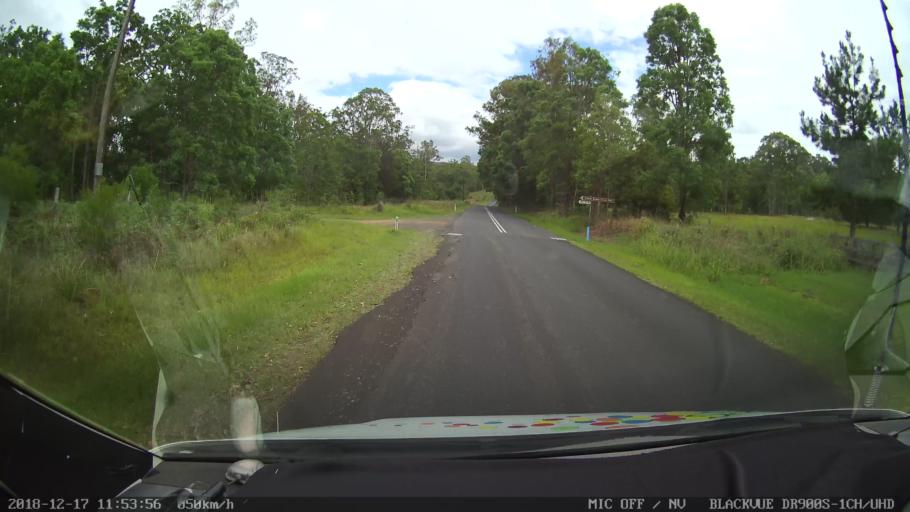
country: AU
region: New South Wales
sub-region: Kyogle
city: Kyogle
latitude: -28.5707
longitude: 152.5853
